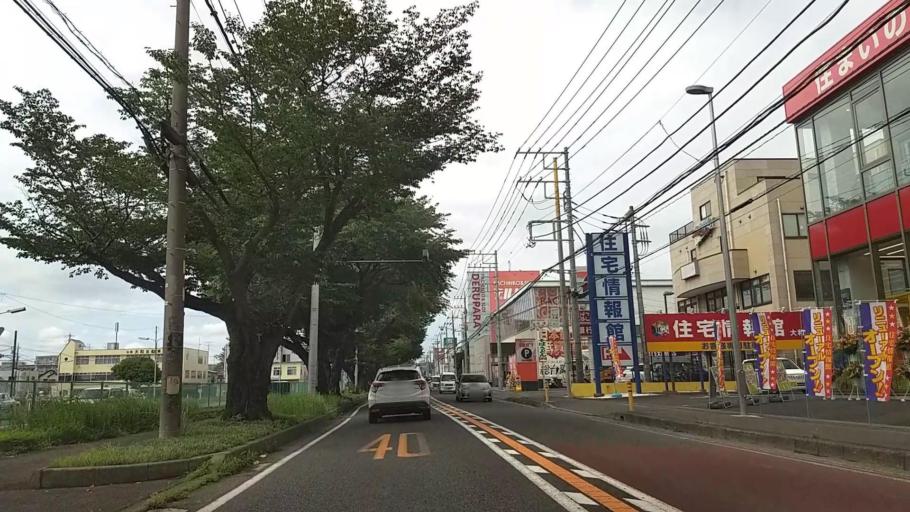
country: JP
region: Kanagawa
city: Minami-rinkan
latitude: 35.4799
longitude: 139.4646
